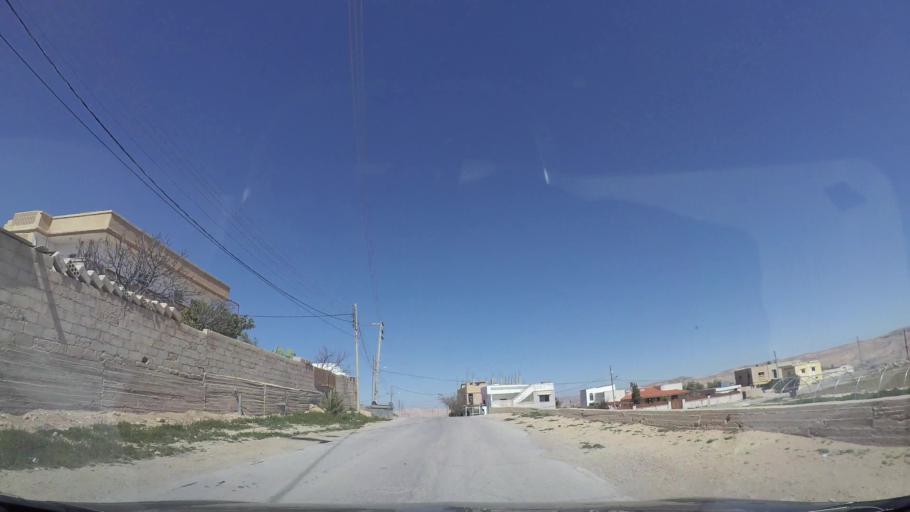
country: JO
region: Tafielah
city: At Tafilah
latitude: 30.8276
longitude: 35.5799
